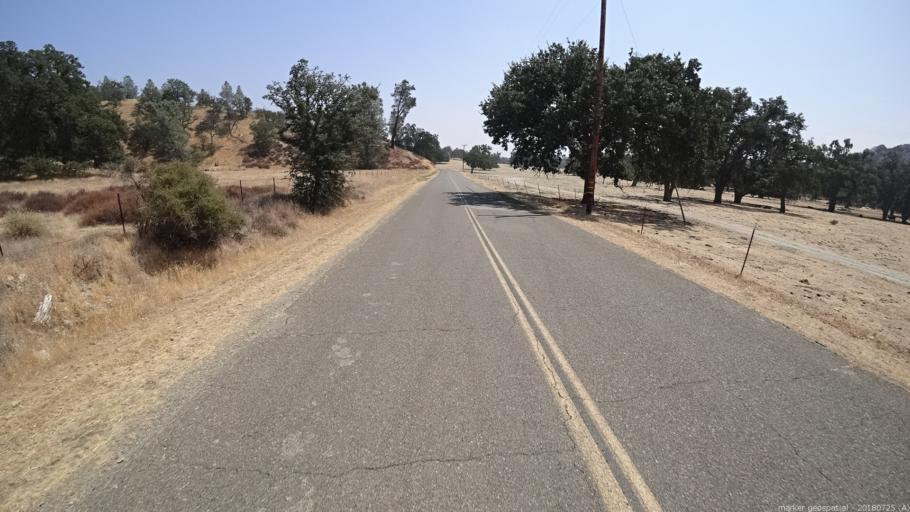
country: US
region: California
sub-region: Fresno County
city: Coalinga
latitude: 35.9137
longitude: -120.4812
